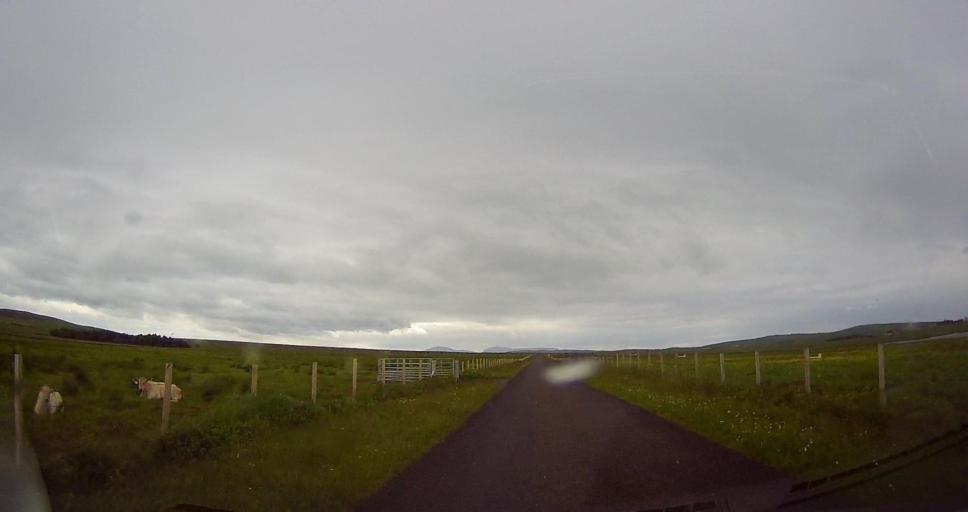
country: GB
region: Scotland
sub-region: Orkney Islands
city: Stromness
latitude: 59.1073
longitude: -3.2548
